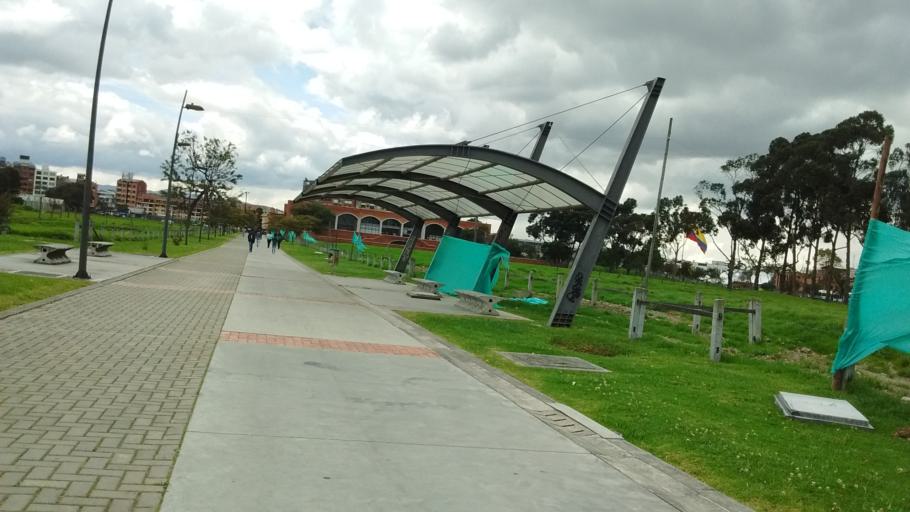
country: CO
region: Bogota D.C.
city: Bogota
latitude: 4.6383
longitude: -74.0890
